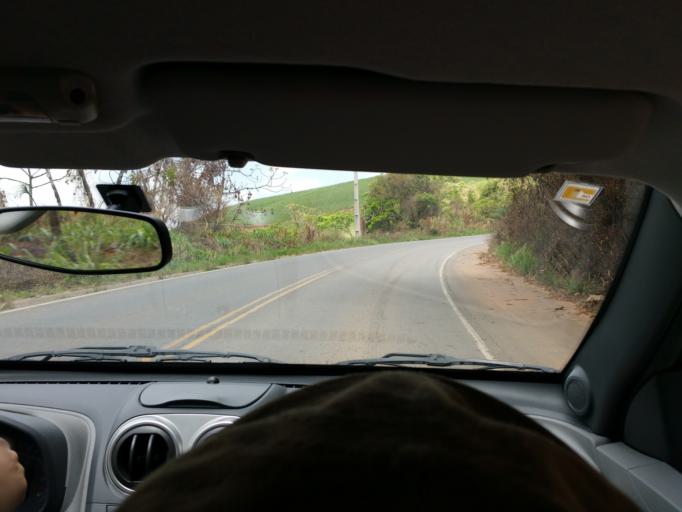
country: BR
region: Pernambuco
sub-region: Sirinhaem
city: Sirinhaem
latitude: -8.6220
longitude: -35.1264
